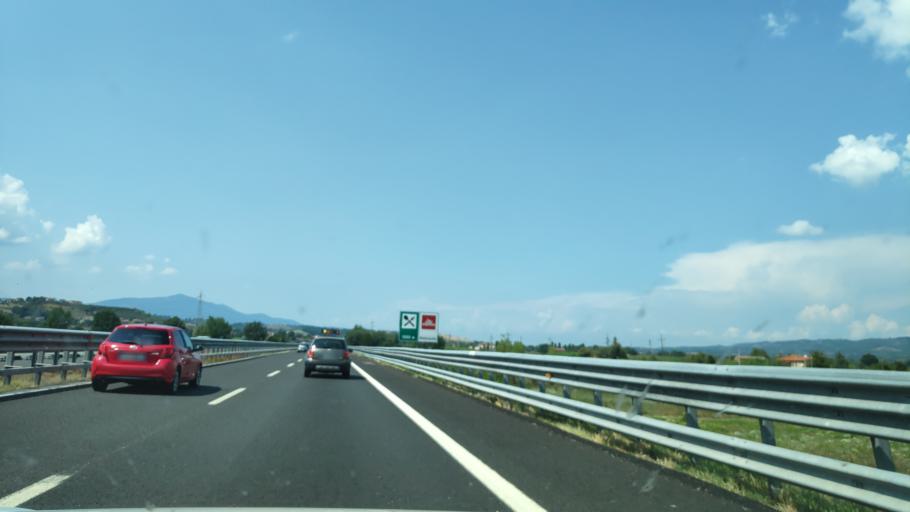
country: IT
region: Umbria
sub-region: Provincia di Terni
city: Fabro Scalo
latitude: 42.8647
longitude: 12.0322
